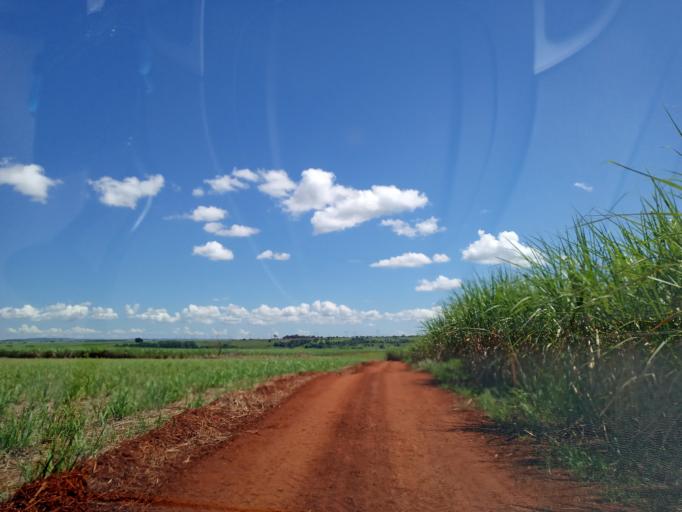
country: BR
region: Goias
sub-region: Itumbiara
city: Itumbiara
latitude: -18.4048
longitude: -49.1286
